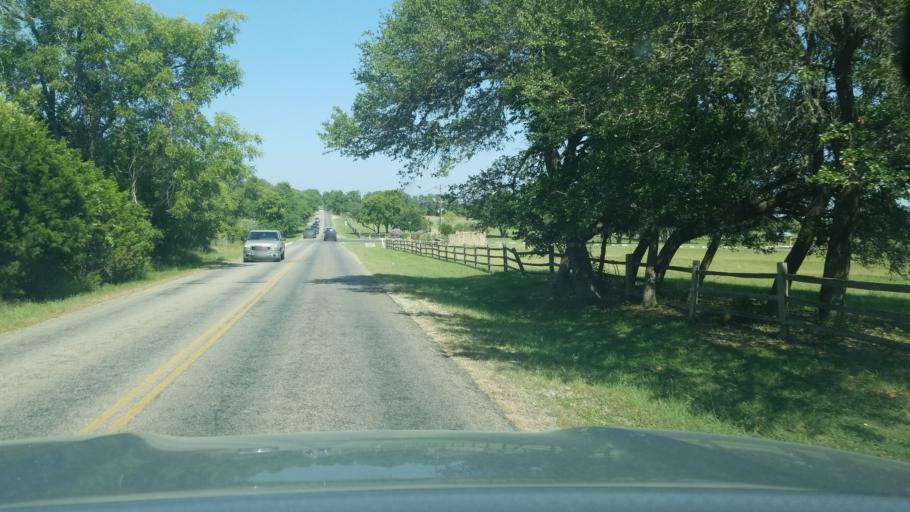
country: US
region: Texas
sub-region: Bexar County
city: Fair Oaks Ranch
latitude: 29.7867
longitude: -98.6751
